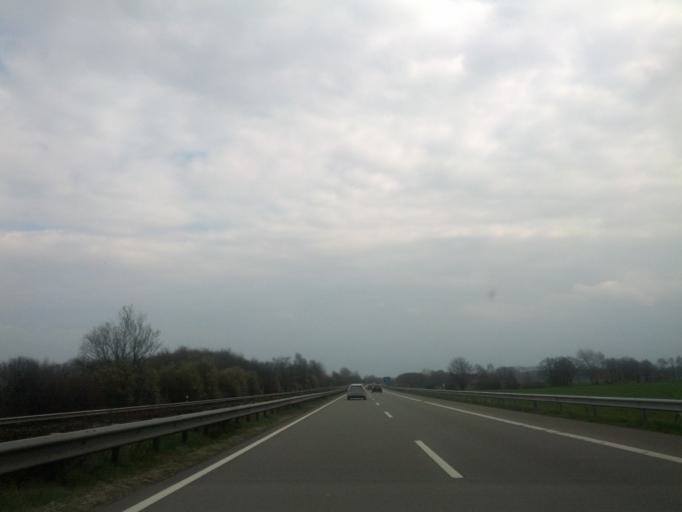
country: DE
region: Lower Saxony
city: Westerstede
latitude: 53.2854
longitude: 7.8818
